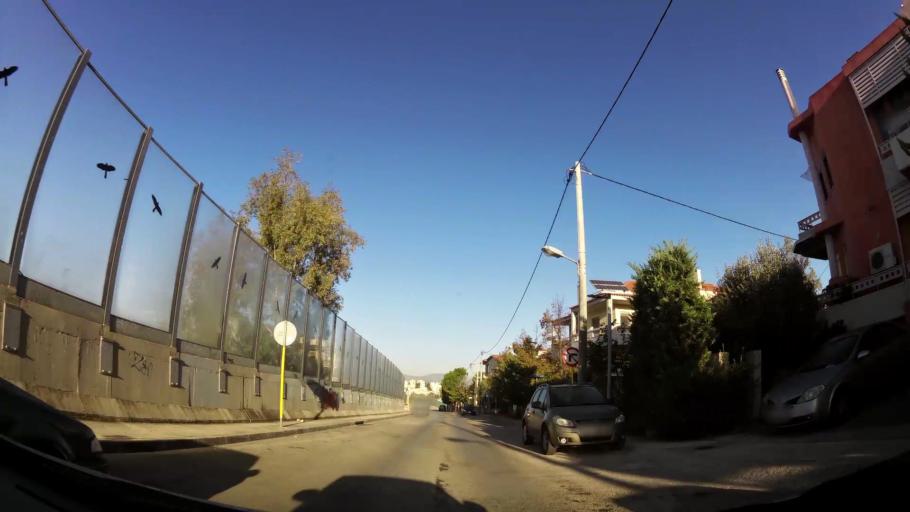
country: GR
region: Attica
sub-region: Nomarchia Athinas
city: Marousi
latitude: 38.0467
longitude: 23.7898
